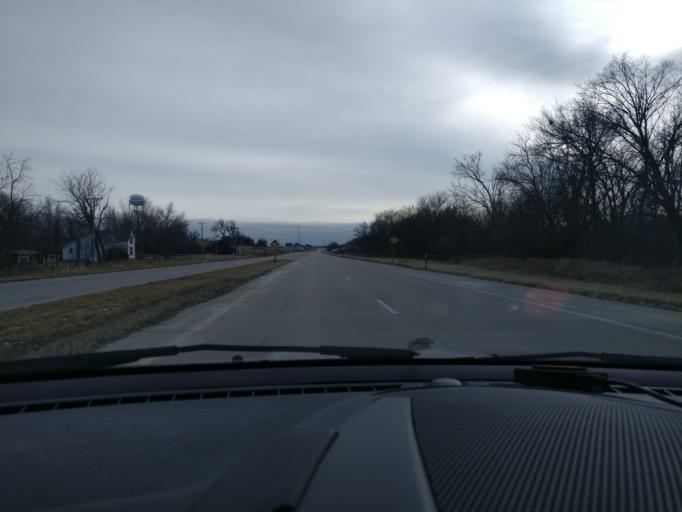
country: US
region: Nebraska
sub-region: Saunders County
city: Wahoo
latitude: 41.0651
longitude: -96.6404
